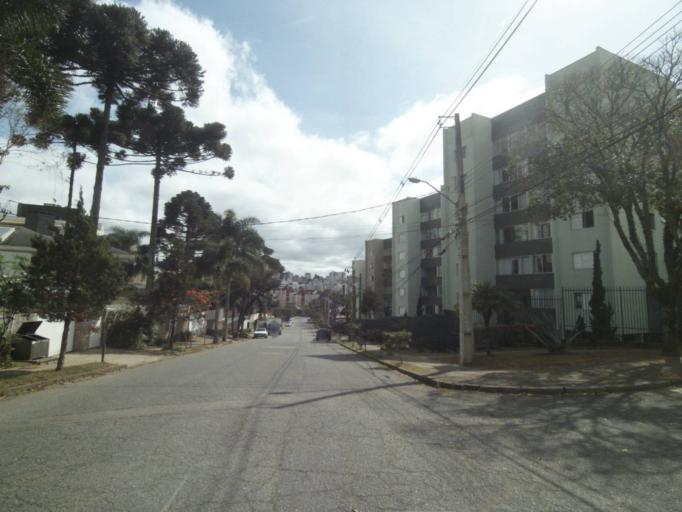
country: BR
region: Parana
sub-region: Curitiba
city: Curitiba
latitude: -25.4663
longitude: -49.2826
